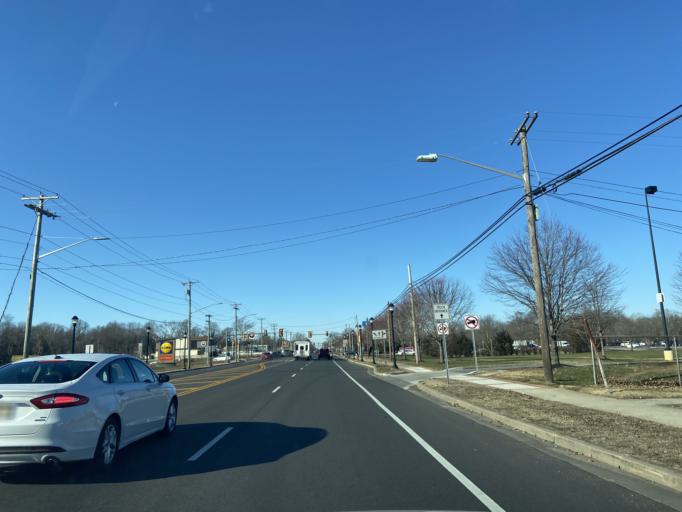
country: US
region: New Jersey
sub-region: Cumberland County
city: Vineland
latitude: 39.4872
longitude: -75.0458
